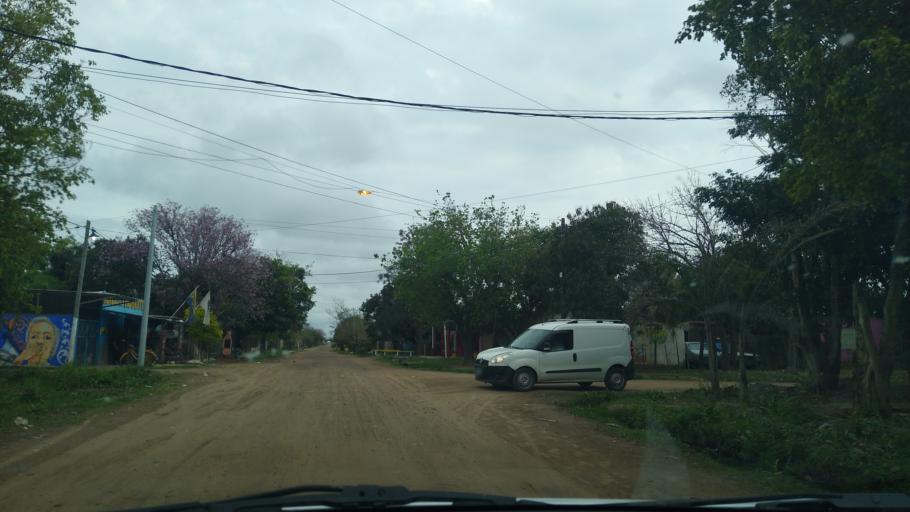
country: AR
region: Chaco
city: Barranqueras
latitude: -27.4754
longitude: -58.9198
